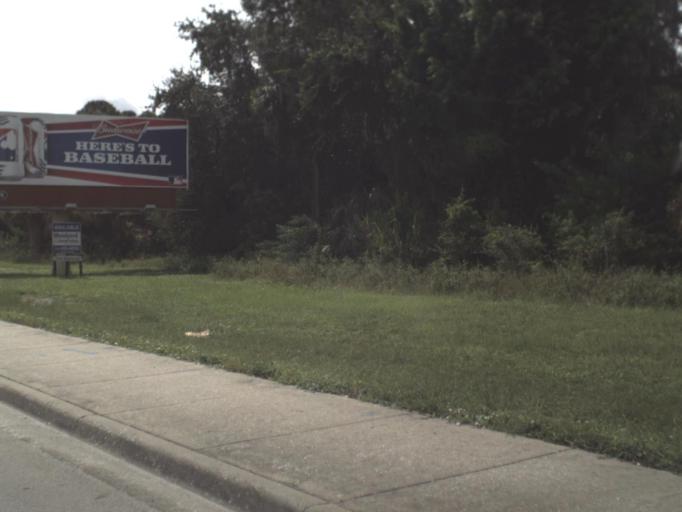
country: US
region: Florida
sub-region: Lee County
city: Palmona Park
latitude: 26.6813
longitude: -81.8835
